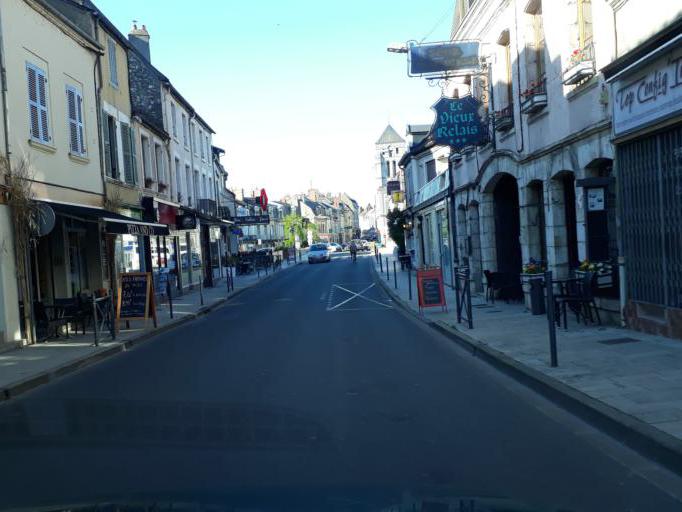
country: FR
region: Bourgogne
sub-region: Departement de la Nievre
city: Cosne-Cours-sur-Loire
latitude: 47.4091
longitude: 2.9238
